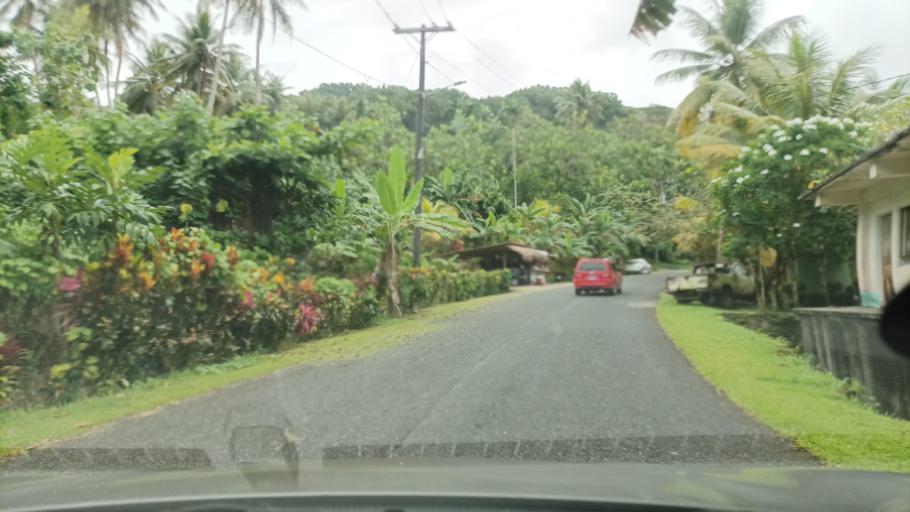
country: FM
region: Pohnpei
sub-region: Kolonia Municipality
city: Kolonia
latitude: 6.9638
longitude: 158.2610
